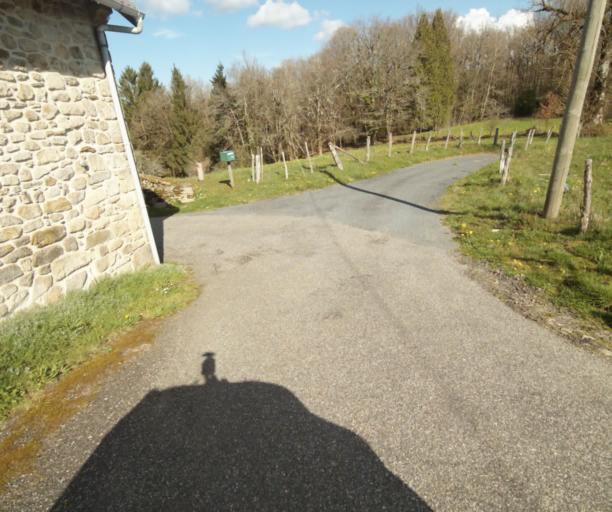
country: FR
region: Limousin
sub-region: Departement de la Correze
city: Laguenne
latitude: 45.2376
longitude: 1.9061
